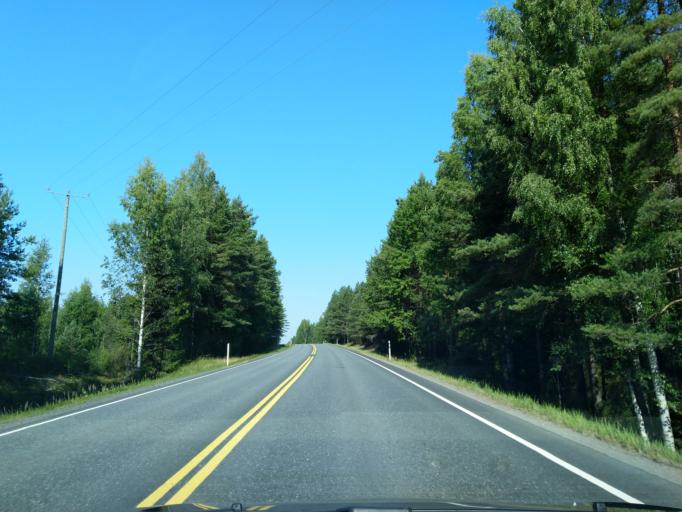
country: FI
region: Haeme
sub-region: Forssa
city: Humppila
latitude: 60.9647
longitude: 23.3096
